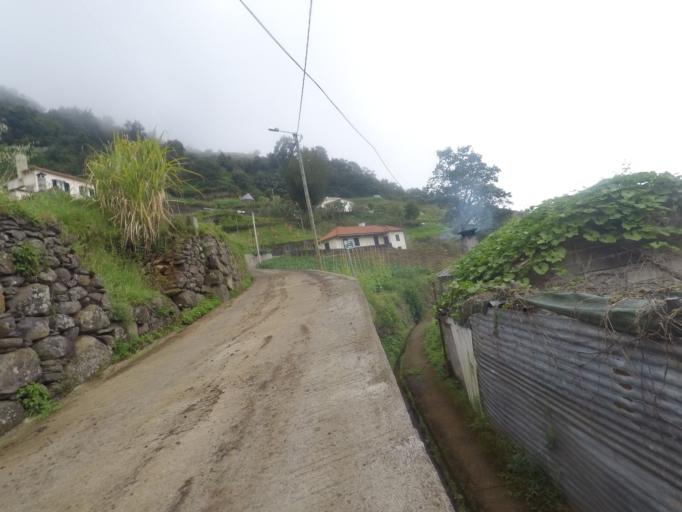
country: PT
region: Madeira
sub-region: Santana
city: Santana
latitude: 32.7726
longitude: -16.8790
